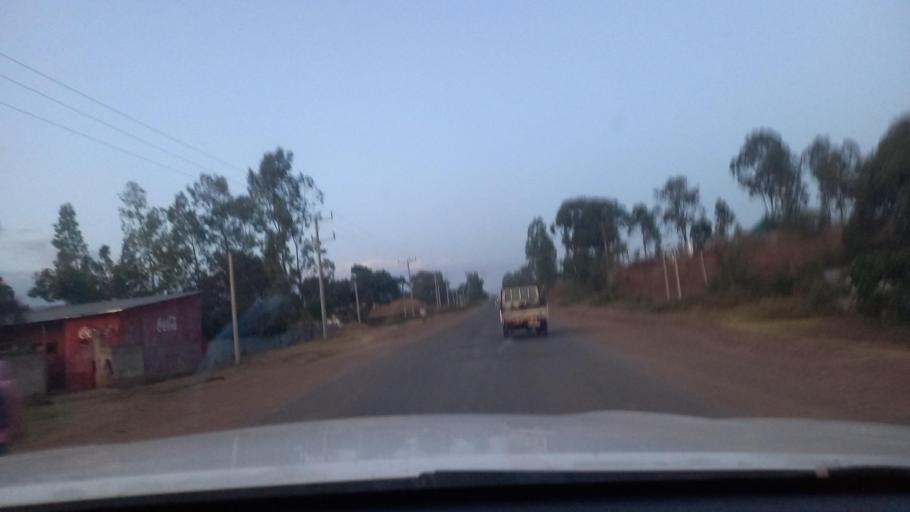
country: ET
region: Southern Nations, Nationalities, and People's Region
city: Butajira
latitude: 7.8596
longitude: 38.1911
